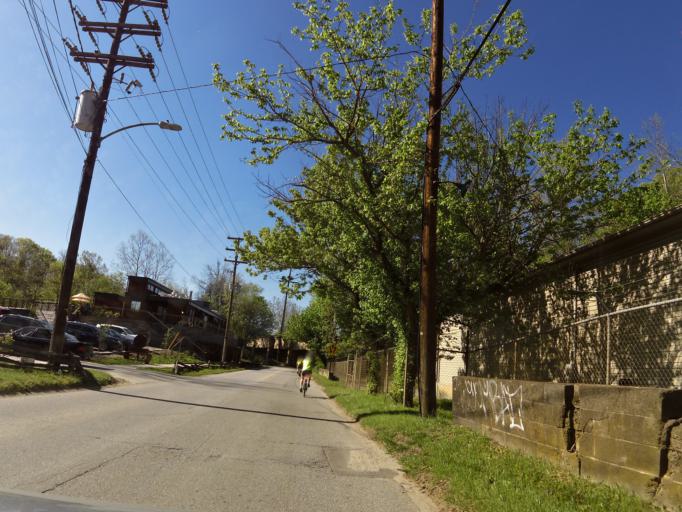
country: US
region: North Carolina
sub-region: Buncombe County
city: Asheville
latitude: 35.5914
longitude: -82.5714
